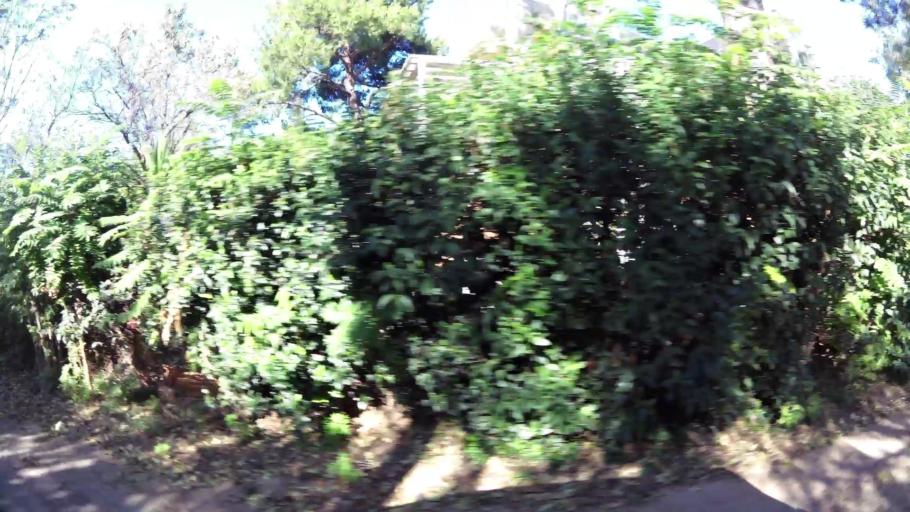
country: GR
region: Attica
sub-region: Nomarchia Athinas
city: Ekali
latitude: 38.1194
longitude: 23.8369
